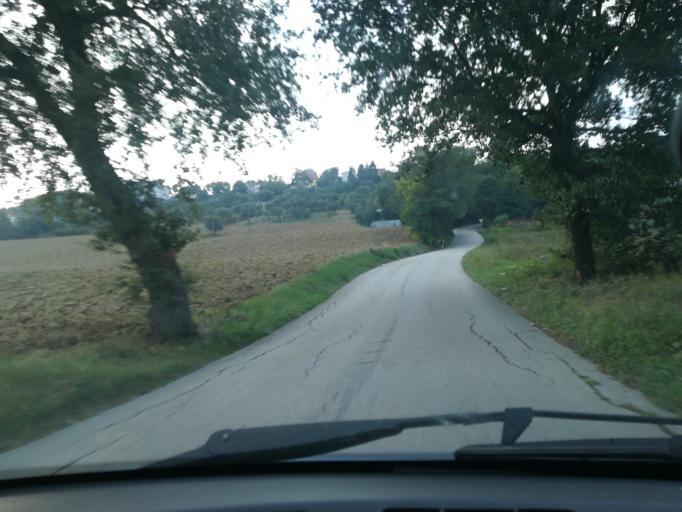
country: IT
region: The Marches
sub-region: Provincia di Macerata
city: Macerata
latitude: 43.3075
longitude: 13.4690
